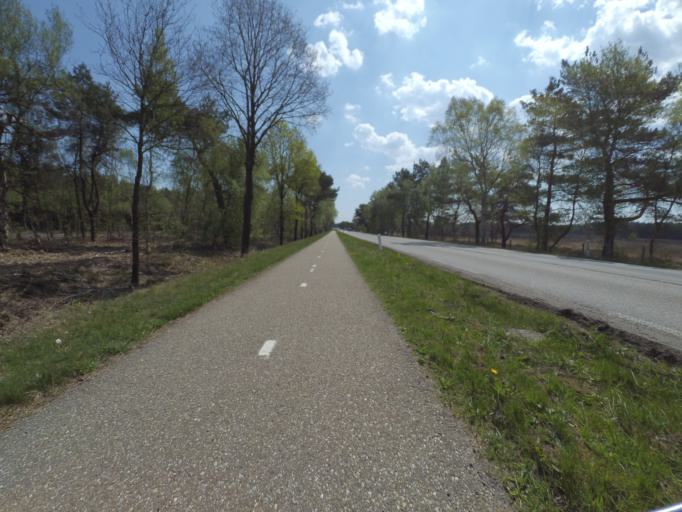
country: NL
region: Gelderland
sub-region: Gemeente Barneveld
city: Garderen
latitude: 52.2857
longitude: 5.6880
